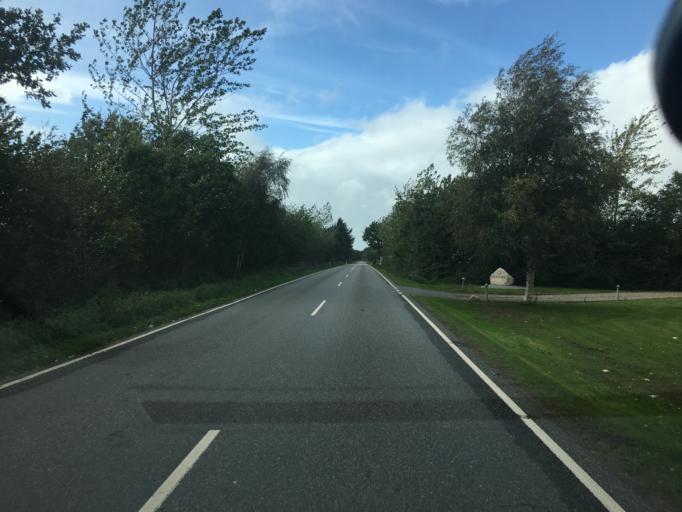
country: DK
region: South Denmark
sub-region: Tonder Kommune
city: Tonder
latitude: 55.0085
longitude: 8.8200
